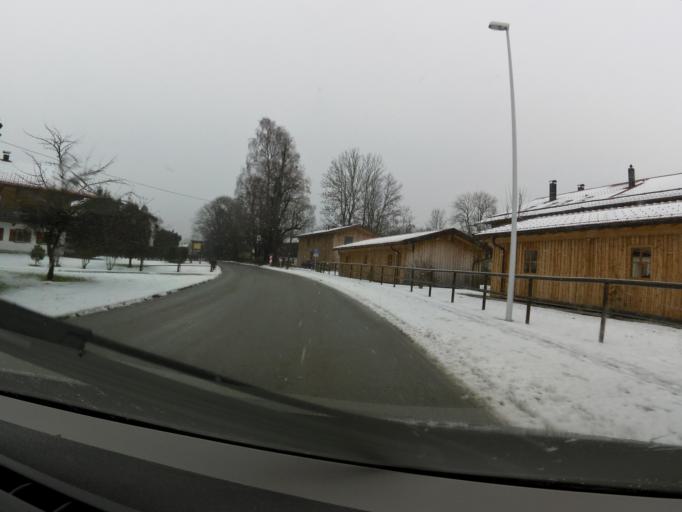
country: DE
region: Bavaria
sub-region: Upper Bavaria
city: Gmund am Tegernsee
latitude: 47.7555
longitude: 11.7122
